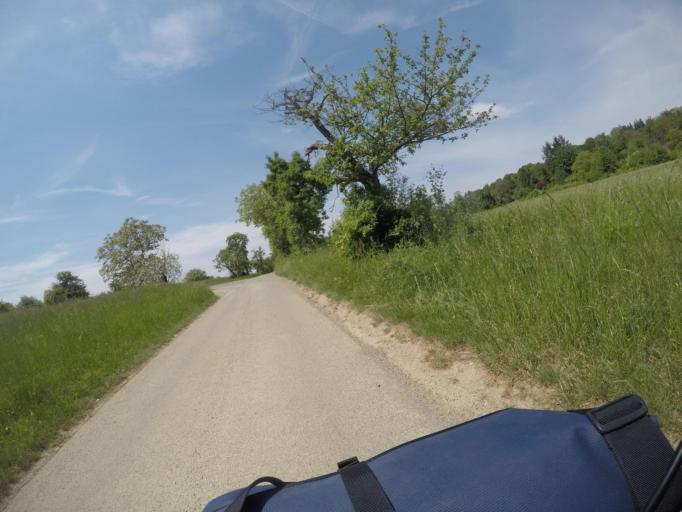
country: DE
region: Baden-Wuerttemberg
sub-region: Karlsruhe Region
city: Konigsbach-Stein
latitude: 48.9367
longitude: 8.6181
